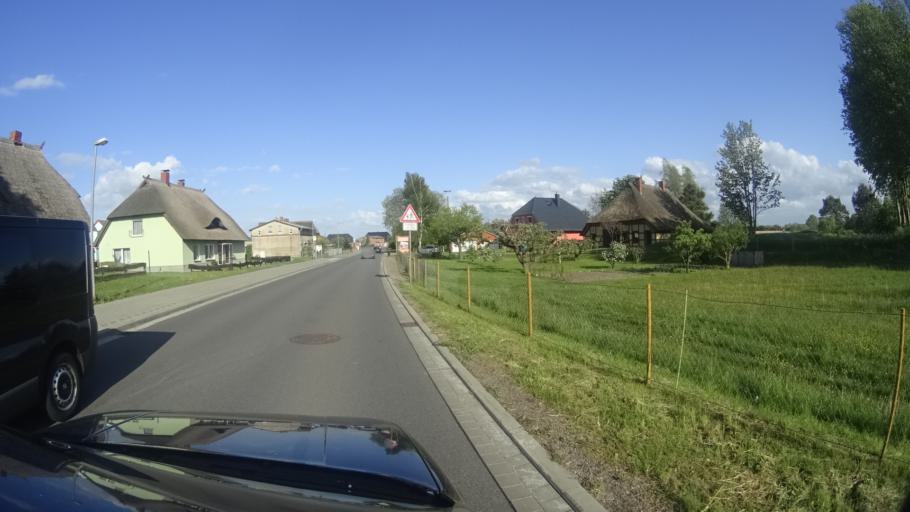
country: DE
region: Mecklenburg-Vorpommern
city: Ostseebad Dierhagen
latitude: 54.2542
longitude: 12.3850
